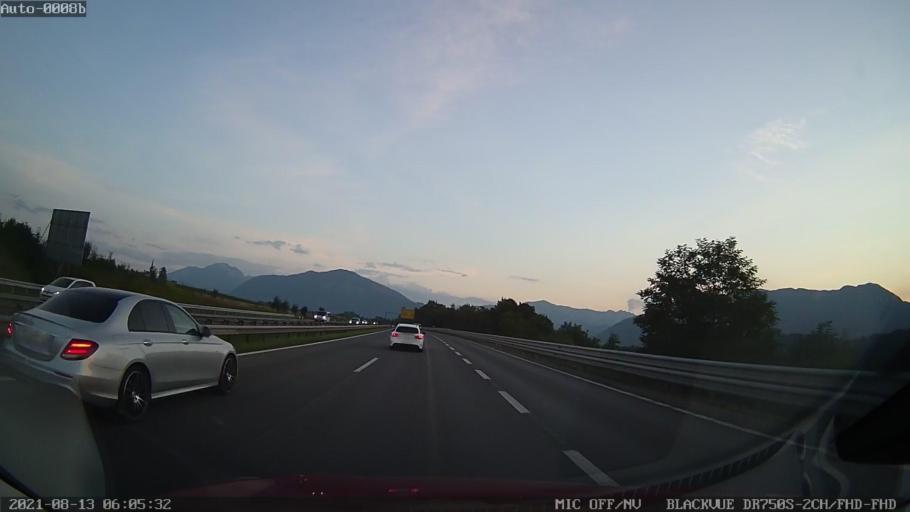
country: SI
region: Naklo
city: Naklo
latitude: 46.3005
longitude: 14.2844
